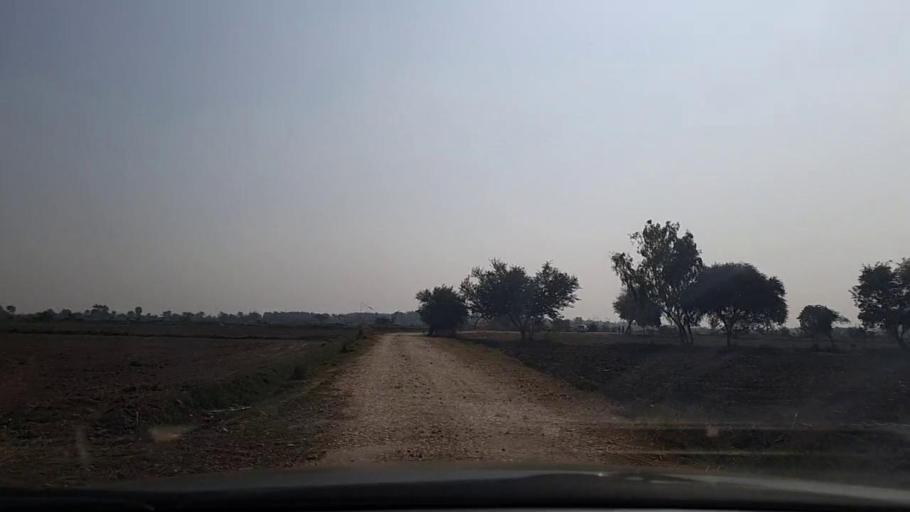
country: PK
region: Sindh
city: Mirpur Sakro
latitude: 24.5664
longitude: 67.7773
